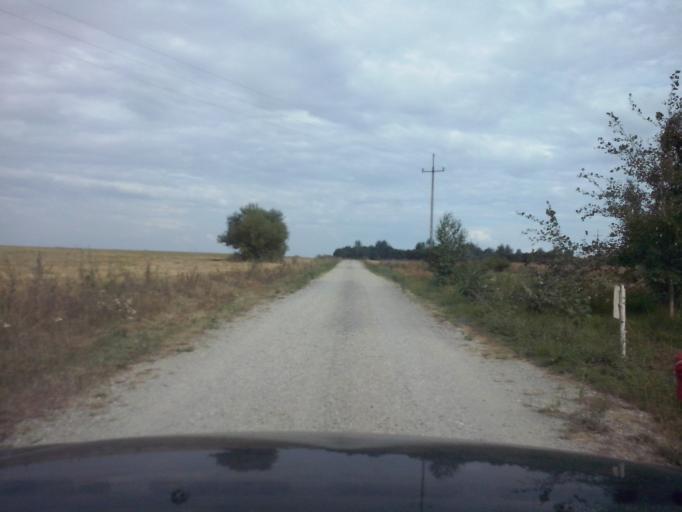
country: PL
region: Swietokrzyskie
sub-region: Powiat kielecki
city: Lagow
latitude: 50.7856
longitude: 21.0833
